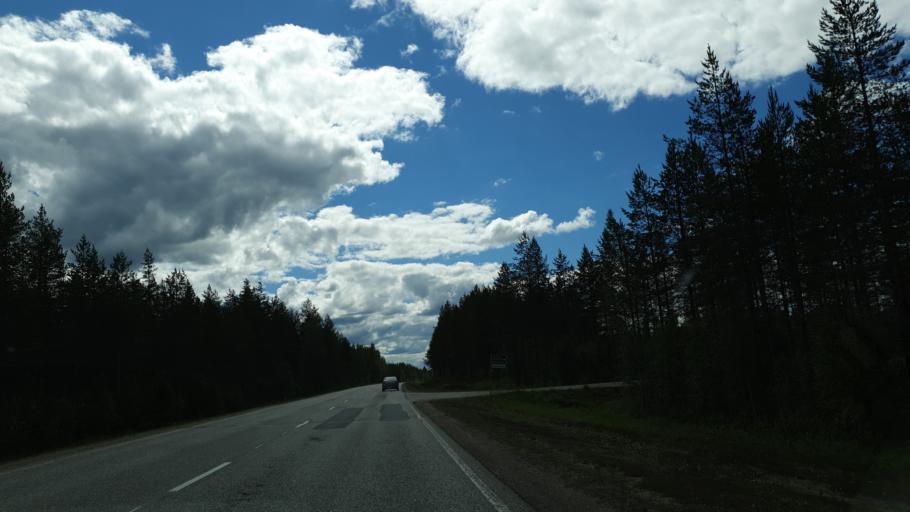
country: FI
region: North Karelia
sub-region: Pielisen Karjala
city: Valtimo
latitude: 63.4537
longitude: 28.7968
